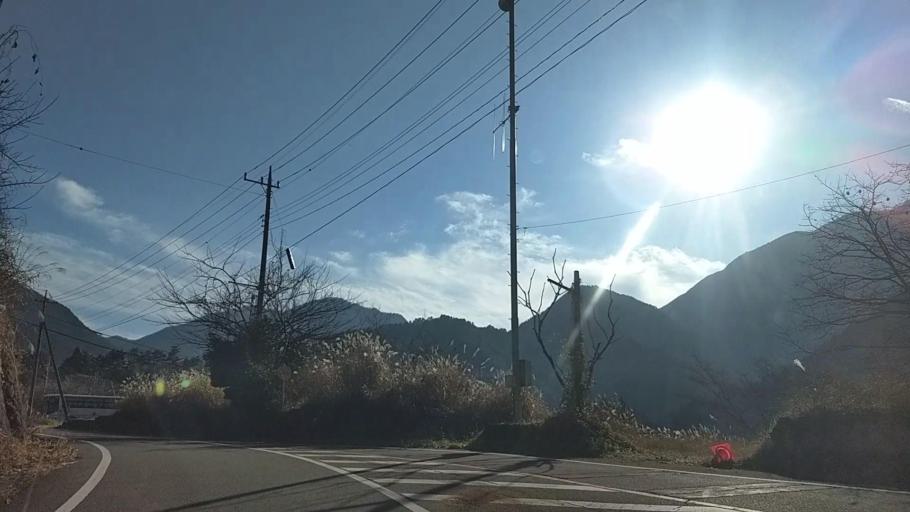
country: JP
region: Yamanashi
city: Uenohara
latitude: 35.5310
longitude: 139.0959
